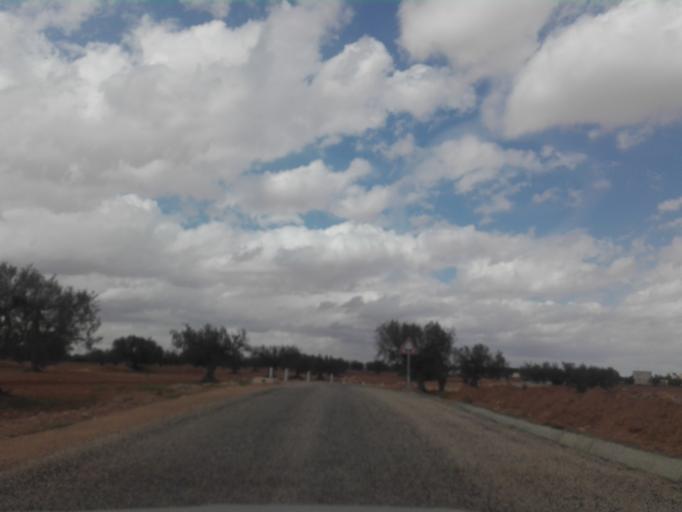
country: TN
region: Safaqis
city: Sfax
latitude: 34.6893
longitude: 10.4489
